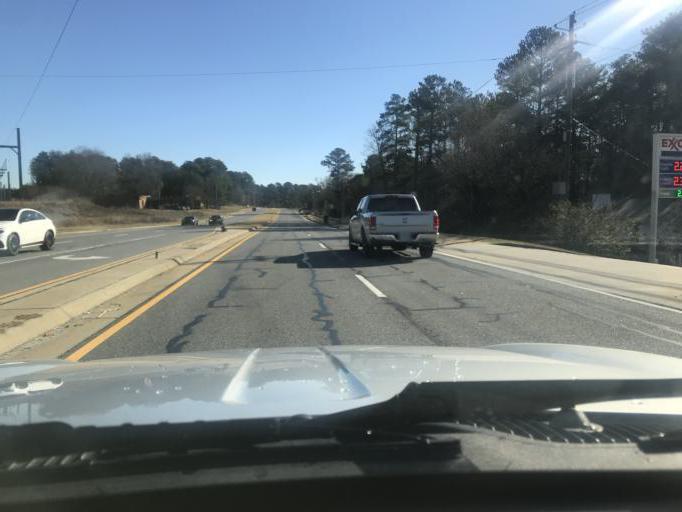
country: US
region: Georgia
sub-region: Gwinnett County
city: Lawrenceville
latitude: 33.9728
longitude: -84.0549
